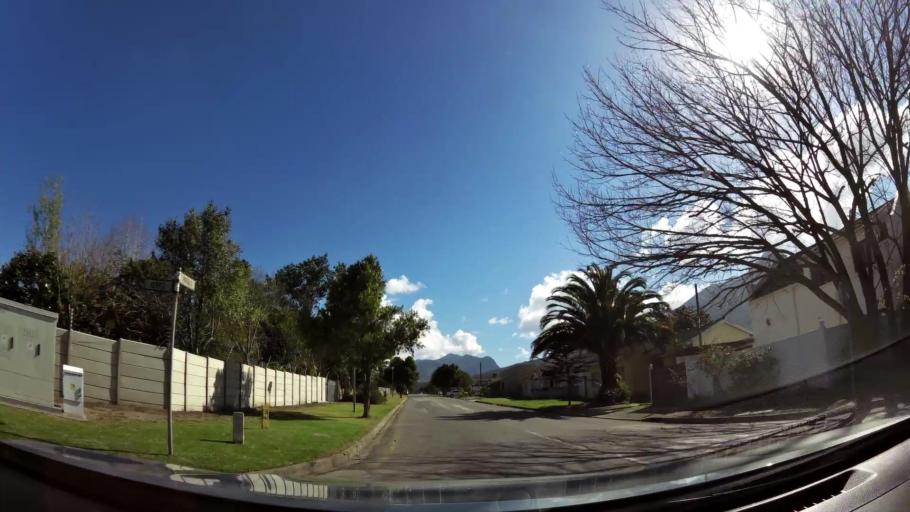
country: ZA
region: Western Cape
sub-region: Eden District Municipality
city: George
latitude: -33.9504
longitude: 22.4687
